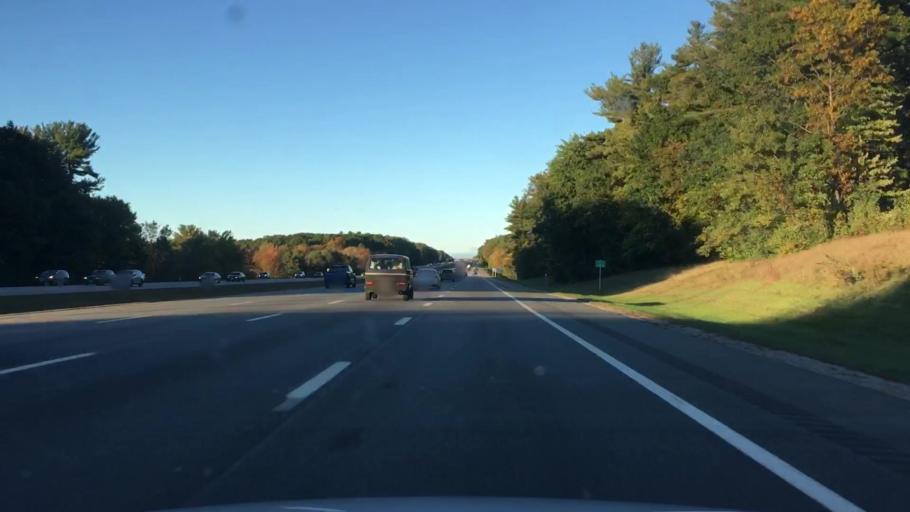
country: US
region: New Hampshire
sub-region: Rockingham County
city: Greenland
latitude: 43.0047
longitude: -70.8409
